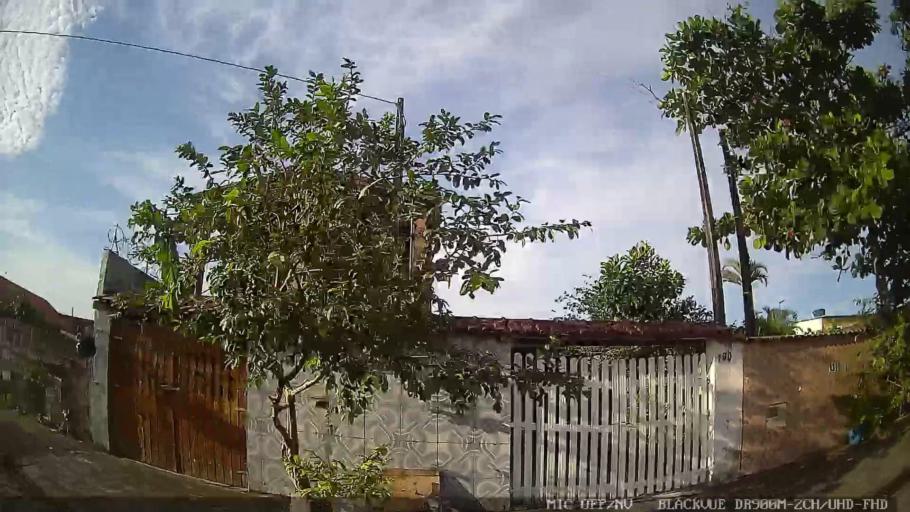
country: BR
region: Sao Paulo
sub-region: Itanhaem
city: Itanhaem
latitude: -24.1611
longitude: -46.7706
